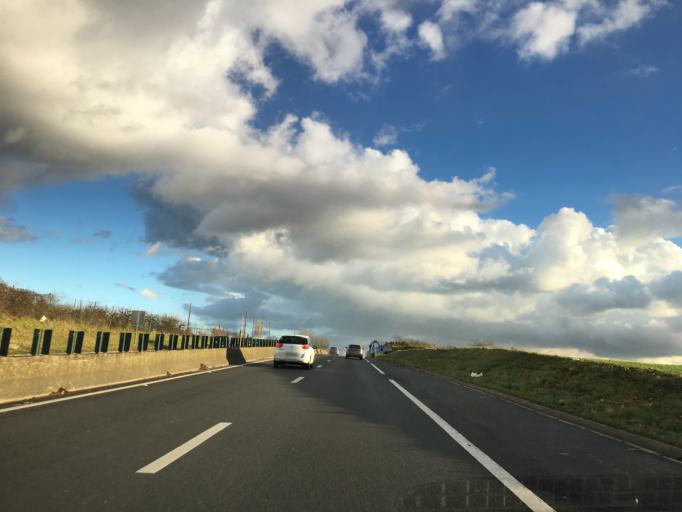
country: FR
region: Ile-de-France
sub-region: Departement du Val-de-Marne
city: La Queue-en-Brie
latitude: 48.7847
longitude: 2.5649
